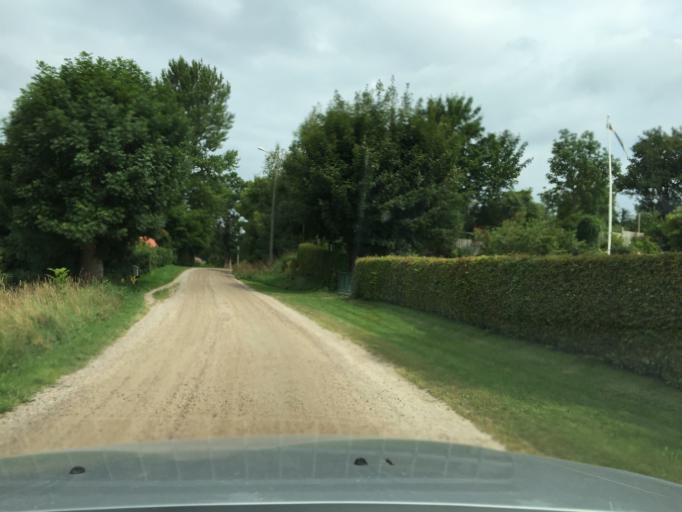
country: SE
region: Skane
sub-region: Hassleholms Kommun
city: Sosdala
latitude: 56.0272
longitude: 13.6842
